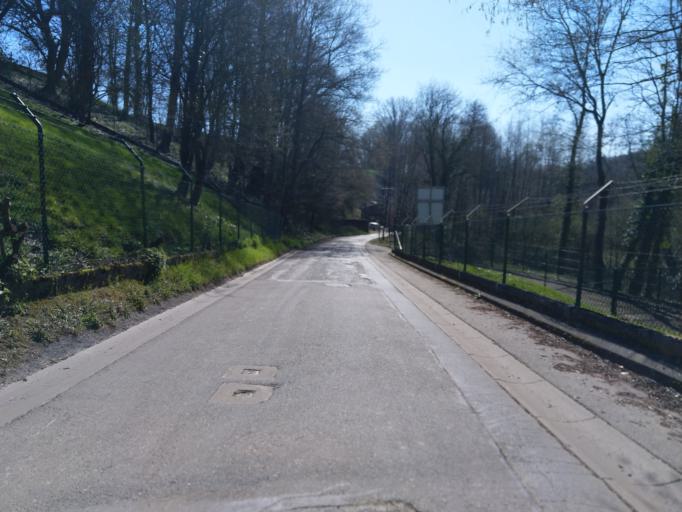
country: BE
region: Wallonia
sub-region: Province du Hainaut
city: Mons
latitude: 50.5106
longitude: 4.0159
